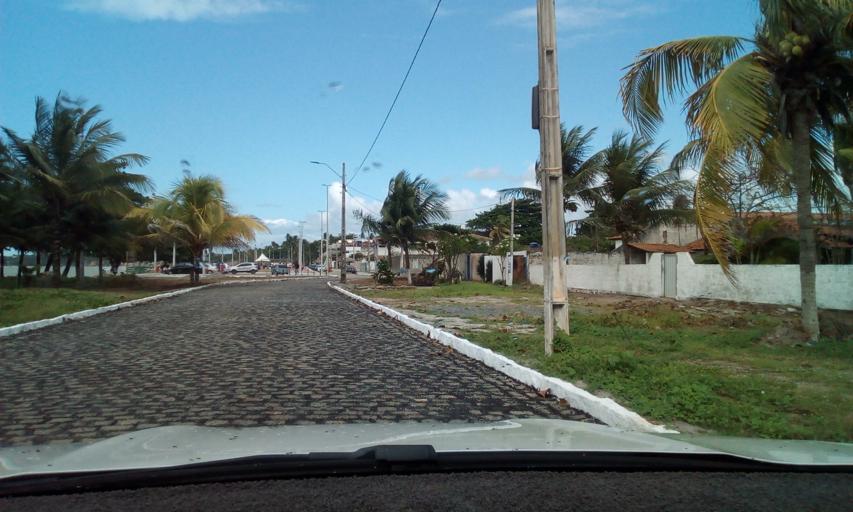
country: BR
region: Paraiba
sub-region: Conde
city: Conde
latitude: -7.2830
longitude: -34.7997
